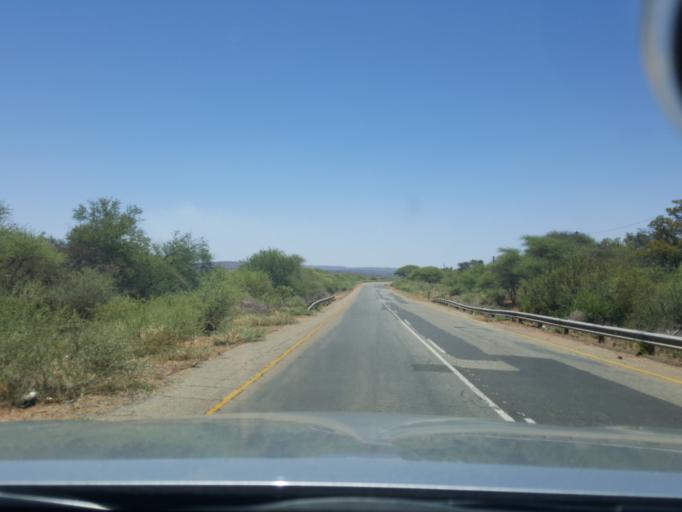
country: ZA
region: North-West
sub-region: Ngaka Modiri Molema District Municipality
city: Zeerust
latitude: -25.3237
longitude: 25.9384
